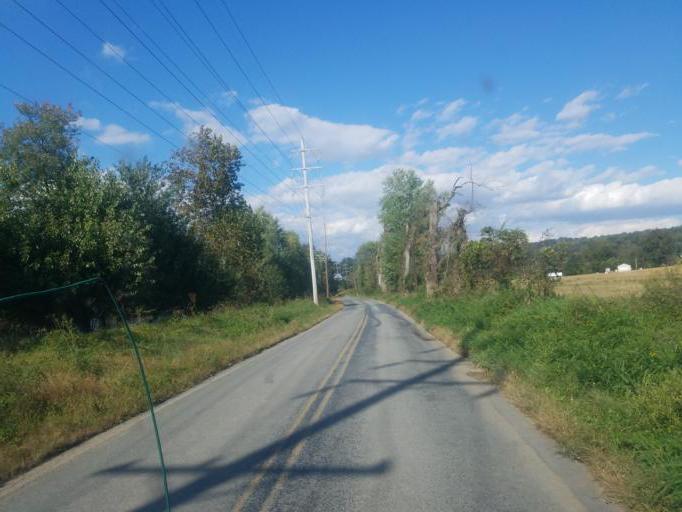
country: US
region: Pennsylvania
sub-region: Dauphin County
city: Middletown
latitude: 40.2026
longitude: -76.7138
